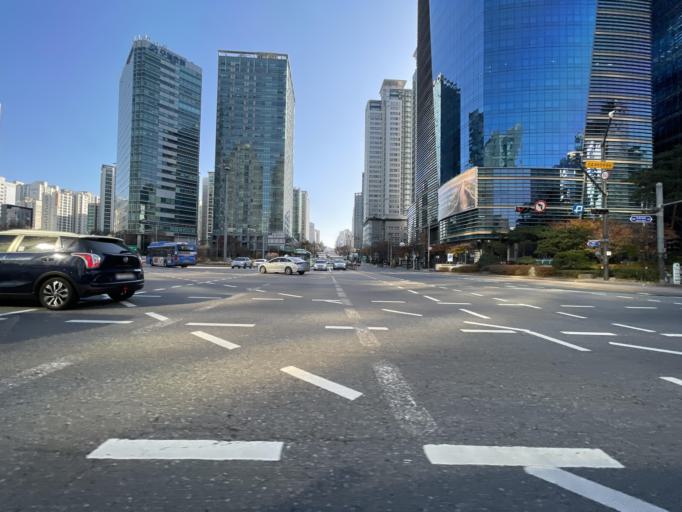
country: KR
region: Seoul
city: Seoul
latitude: 37.5439
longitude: 126.9511
